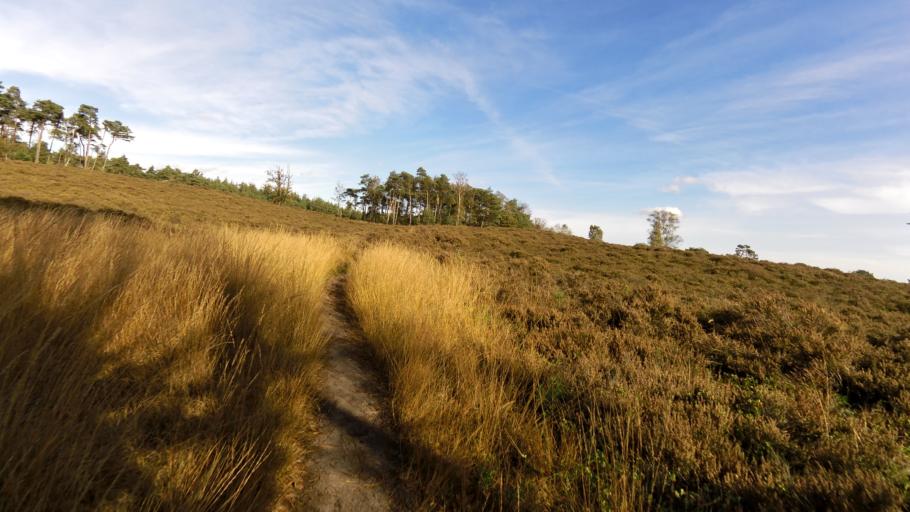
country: NL
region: Gelderland
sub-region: Gemeente Epe
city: Emst
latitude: 52.3423
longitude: 5.9036
